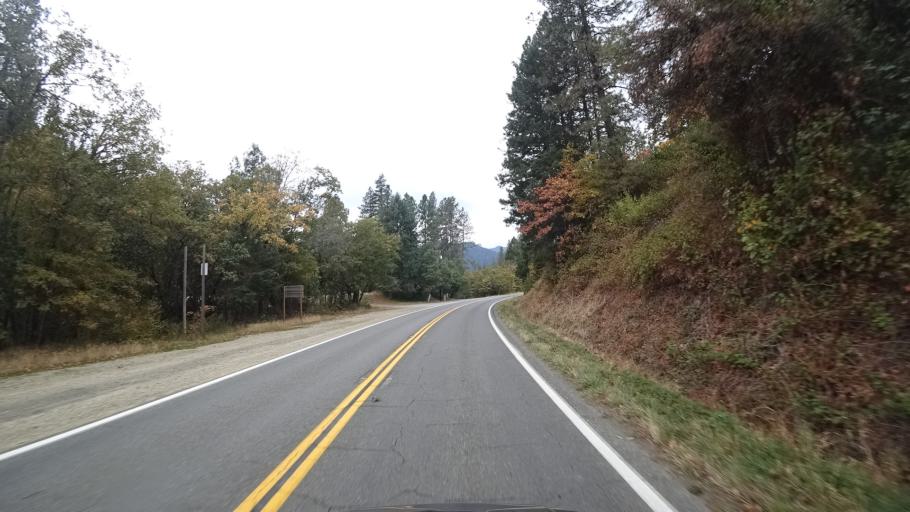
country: US
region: California
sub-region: Siskiyou County
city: Happy Camp
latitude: 41.7887
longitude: -123.3839
